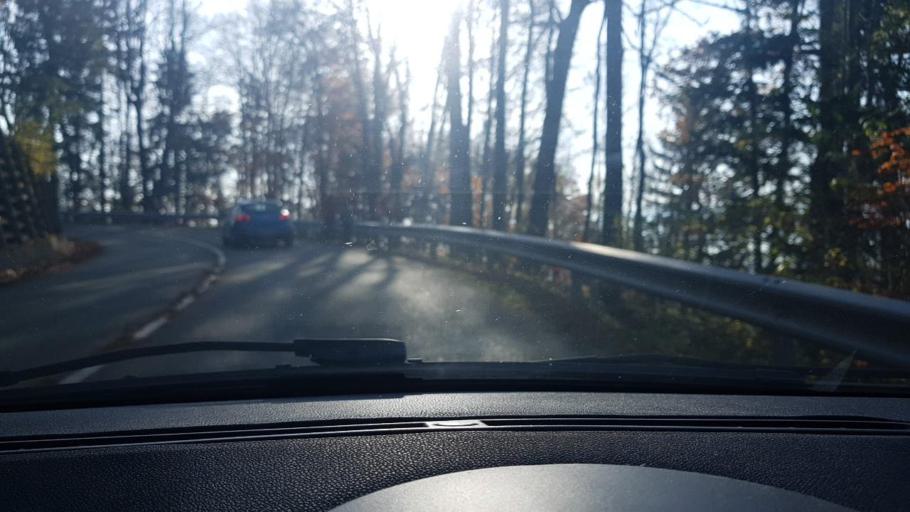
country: SI
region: Kranj
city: Golnik
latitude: 46.3342
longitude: 14.3078
